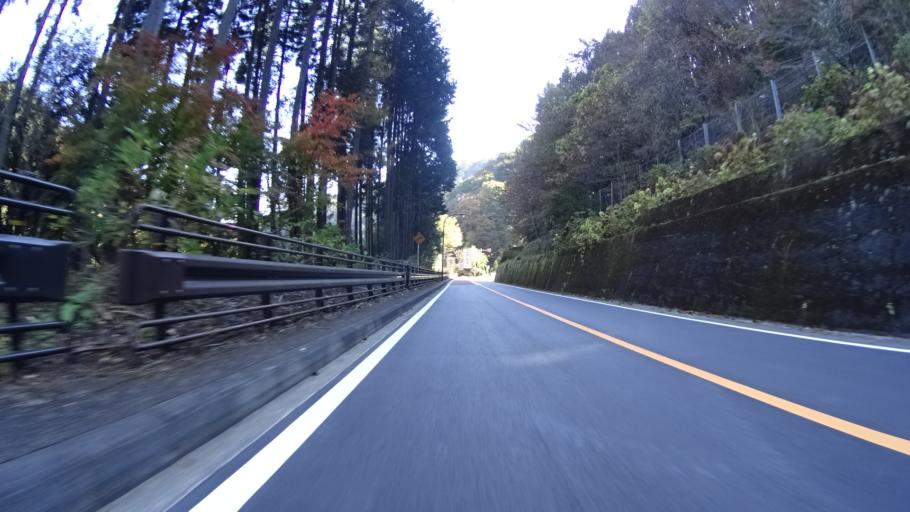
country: JP
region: Yamanashi
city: Uenohara
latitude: 35.7290
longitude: 139.0409
